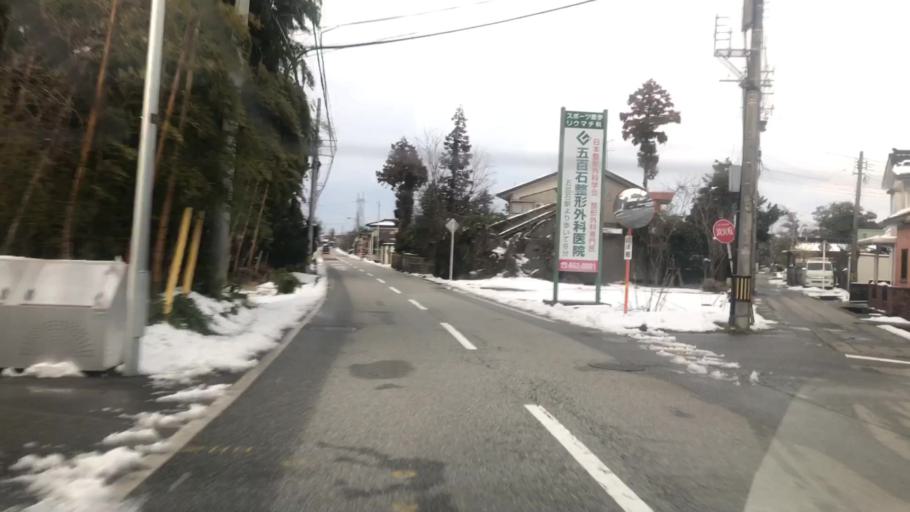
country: JP
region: Toyama
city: Kamiichi
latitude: 36.6927
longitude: 137.3154
